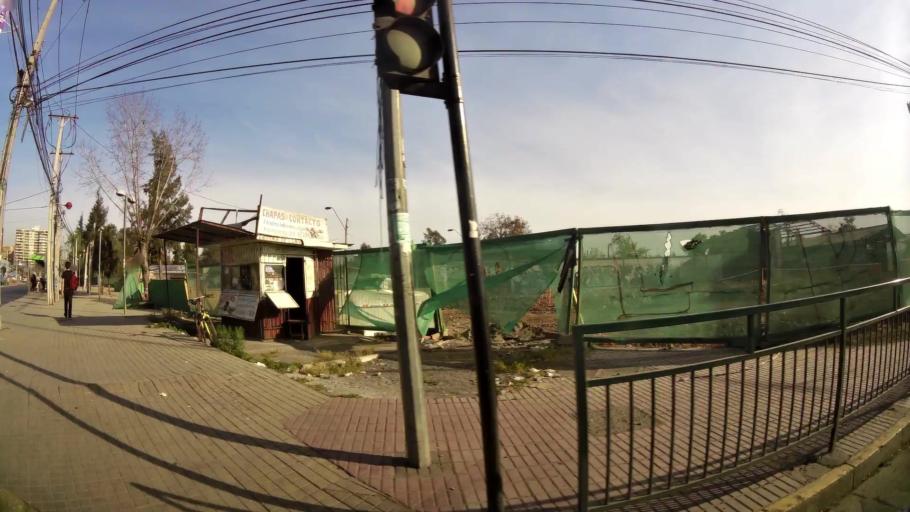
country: CL
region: Santiago Metropolitan
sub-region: Provincia de Santiago
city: Villa Presidente Frei, Nunoa, Santiago, Chile
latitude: -33.5084
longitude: -70.6139
